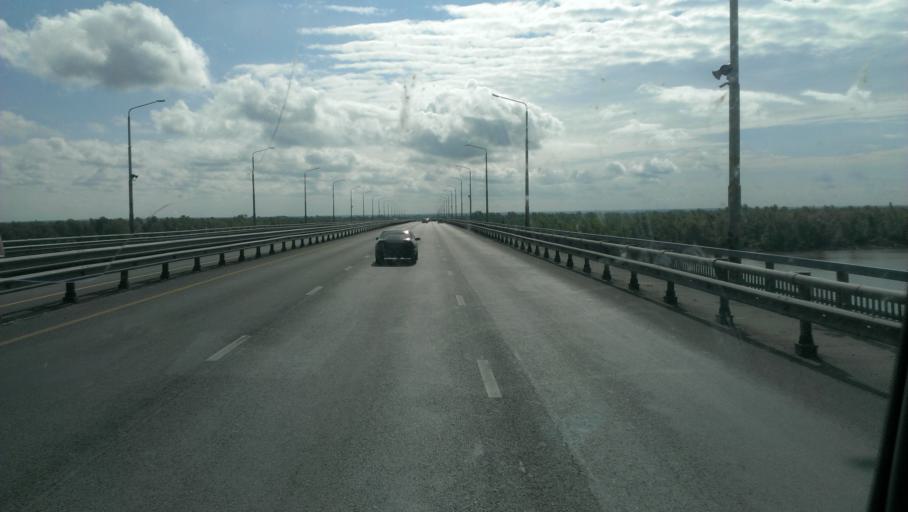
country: RU
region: Altai Krai
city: Zaton
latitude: 53.3240
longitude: 83.8017
